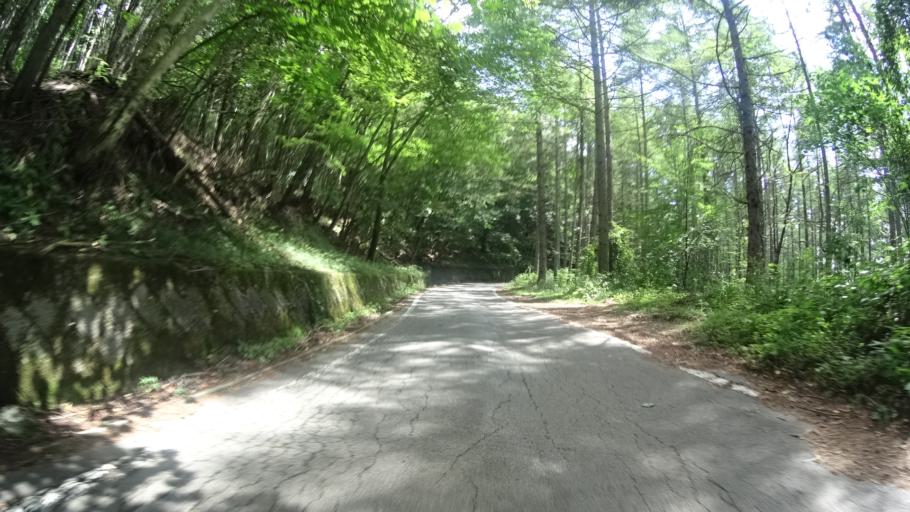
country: JP
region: Yamanashi
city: Enzan
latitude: 35.8301
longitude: 138.6394
